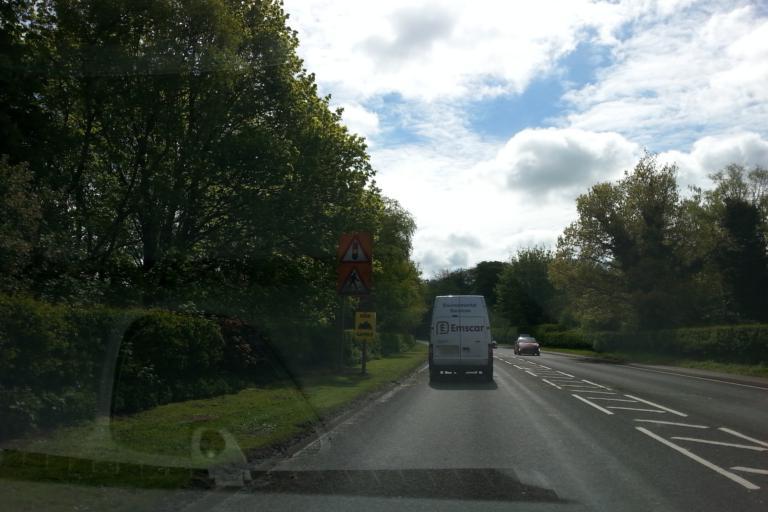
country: GB
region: England
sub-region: Staffordshire
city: Lichfield
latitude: 52.6834
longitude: -1.8422
